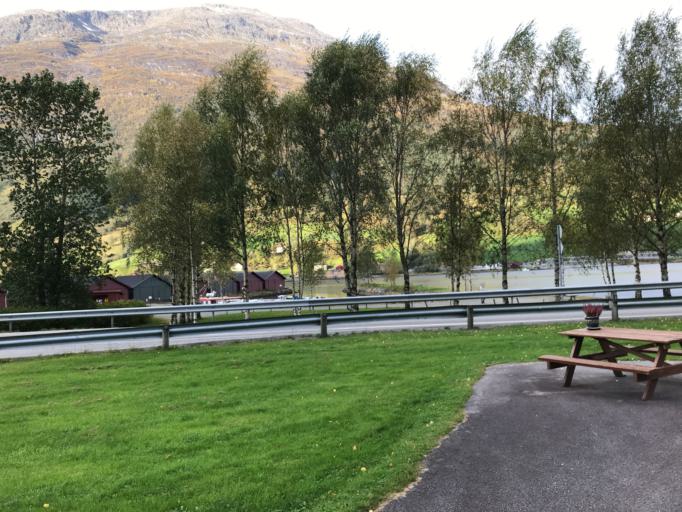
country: NO
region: Sogn og Fjordane
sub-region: Stryn
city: Stryn
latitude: 61.8398
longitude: 6.8114
